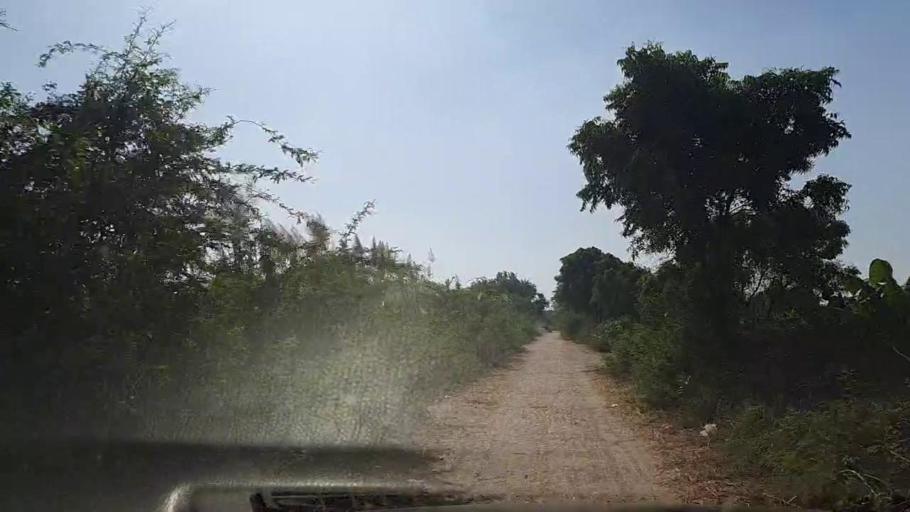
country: PK
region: Sindh
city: Daro Mehar
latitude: 24.8164
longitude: 68.0780
